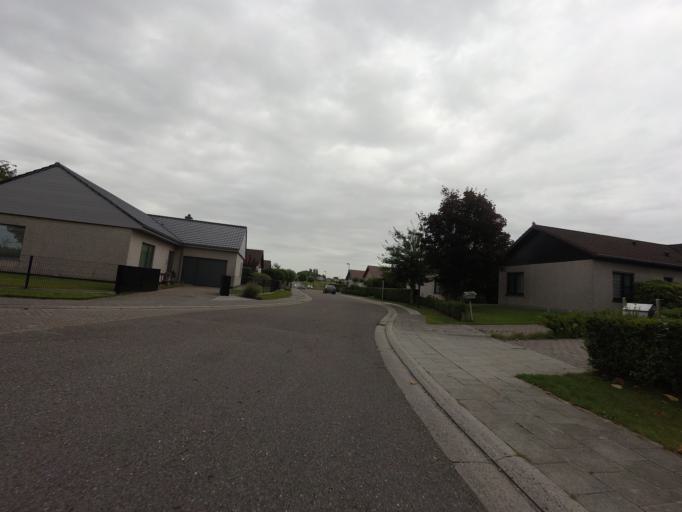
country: BE
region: Flanders
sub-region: Provincie Vlaams-Brabant
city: Meise
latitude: 50.9518
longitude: 4.3373
